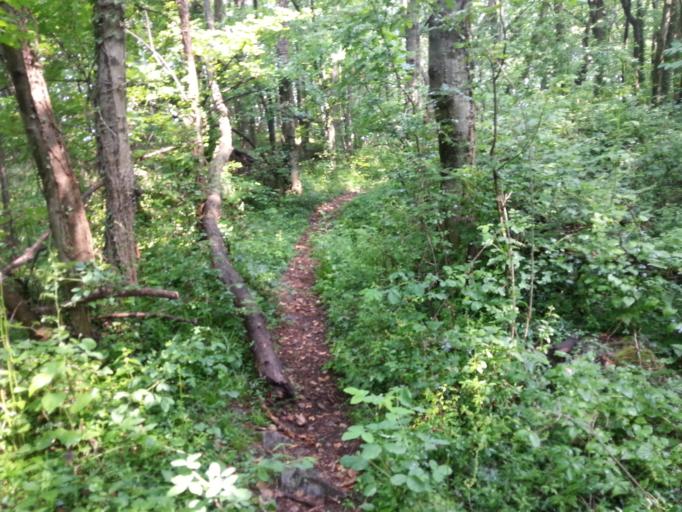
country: IT
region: Lombardy
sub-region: Provincia di Varese
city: Viggiu
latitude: 45.8870
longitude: 8.9094
